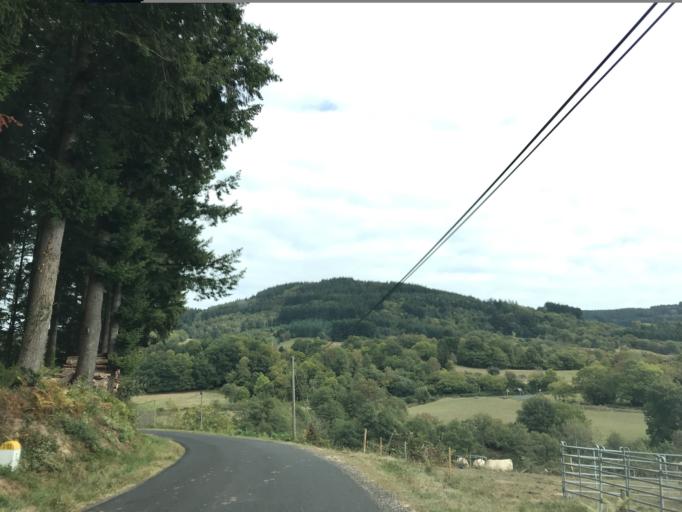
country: FR
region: Auvergne
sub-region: Departement du Puy-de-Dome
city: Celles-sur-Durolle
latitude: 45.8243
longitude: 3.6225
